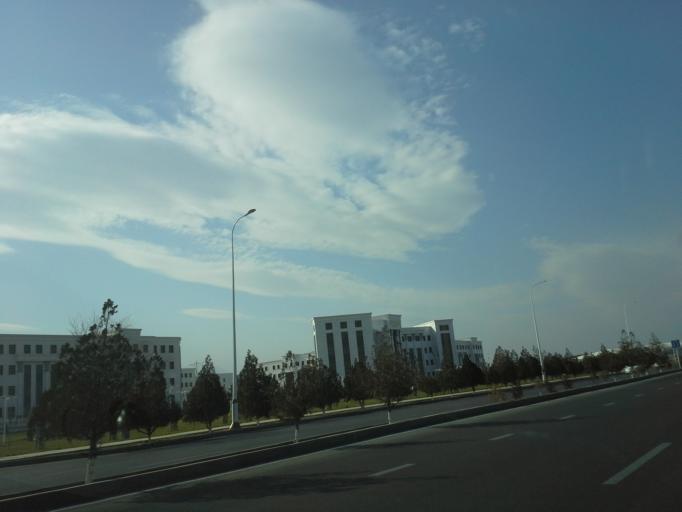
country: TM
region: Ahal
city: Abadan
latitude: 38.0431
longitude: 58.2063
